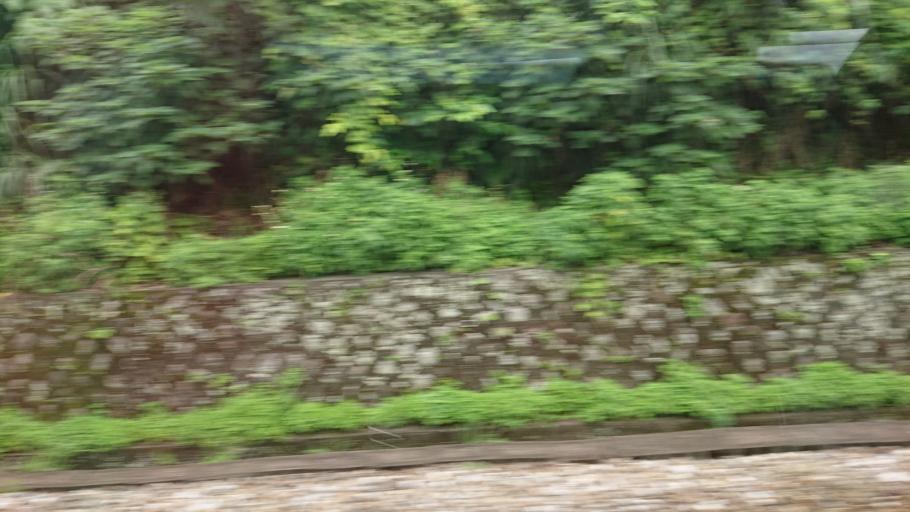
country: TW
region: Taiwan
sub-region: Yilan
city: Yilan
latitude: 24.9072
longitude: 121.8721
